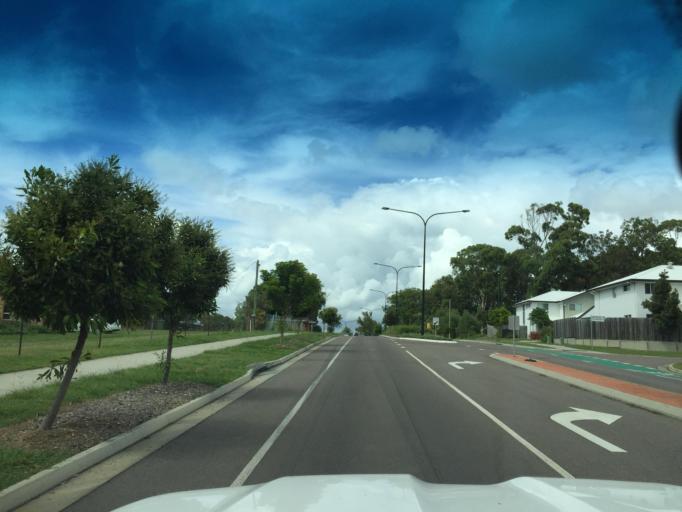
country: AU
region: Queensland
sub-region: Moreton Bay
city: Mango Hill
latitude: -27.2278
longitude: 153.0292
